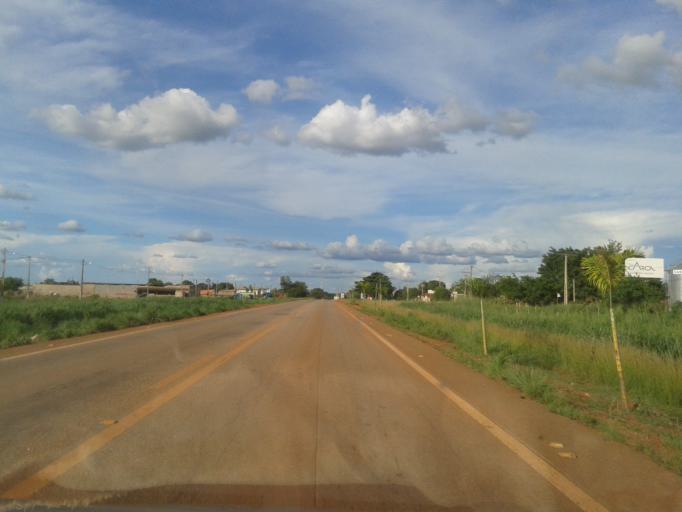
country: BR
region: Goias
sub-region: Crixas
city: Crixas
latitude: -14.1146
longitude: -50.3440
